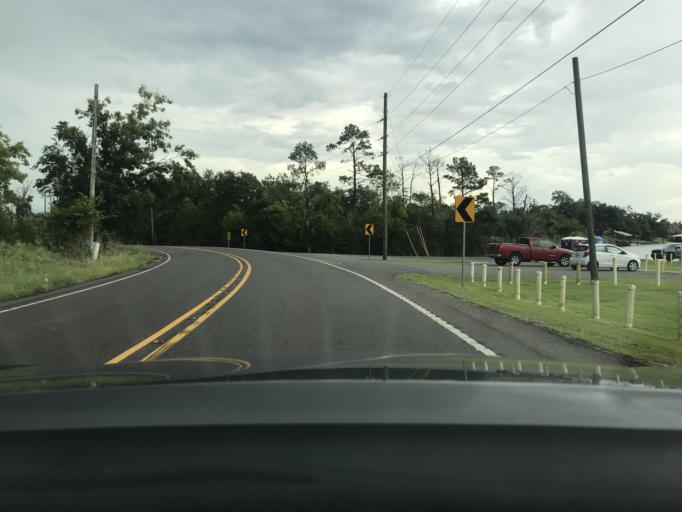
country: US
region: Louisiana
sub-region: Calcasieu Parish
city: Westlake
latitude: 30.2525
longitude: -93.2457
